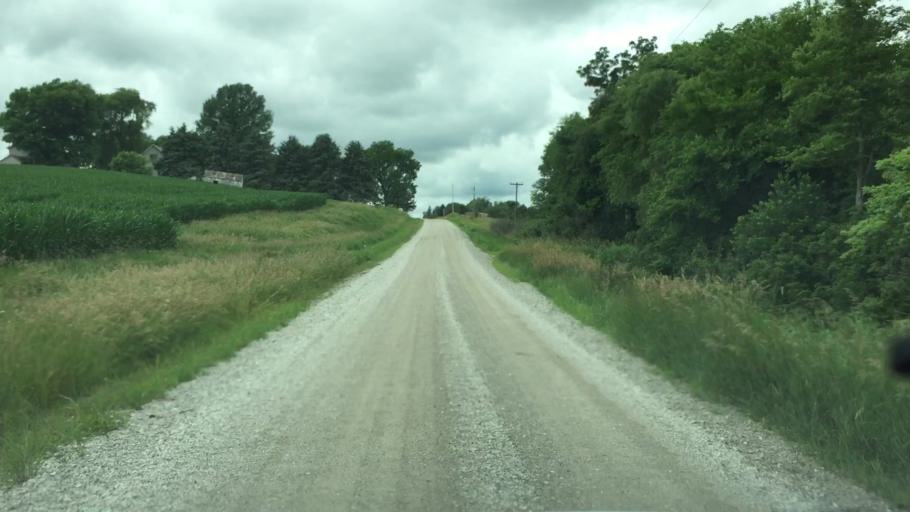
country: US
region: Iowa
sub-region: Jasper County
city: Monroe
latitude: 41.6009
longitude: -93.1439
